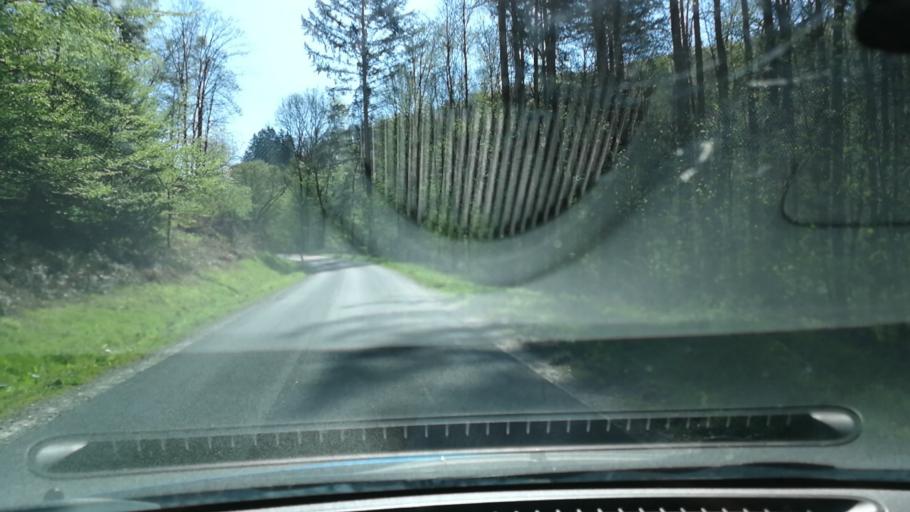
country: DE
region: Lower Saxony
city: Buhren
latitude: 51.5428
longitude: 9.6480
